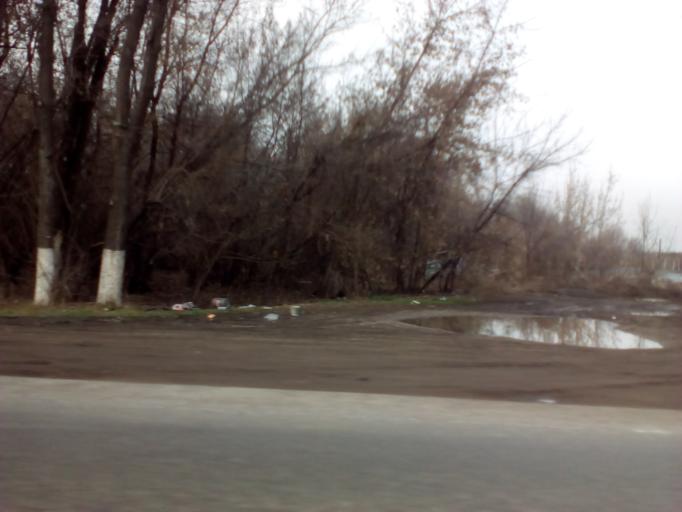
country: KZ
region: Almaty Oblysy
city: Burunday
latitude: 43.2225
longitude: 76.7191
